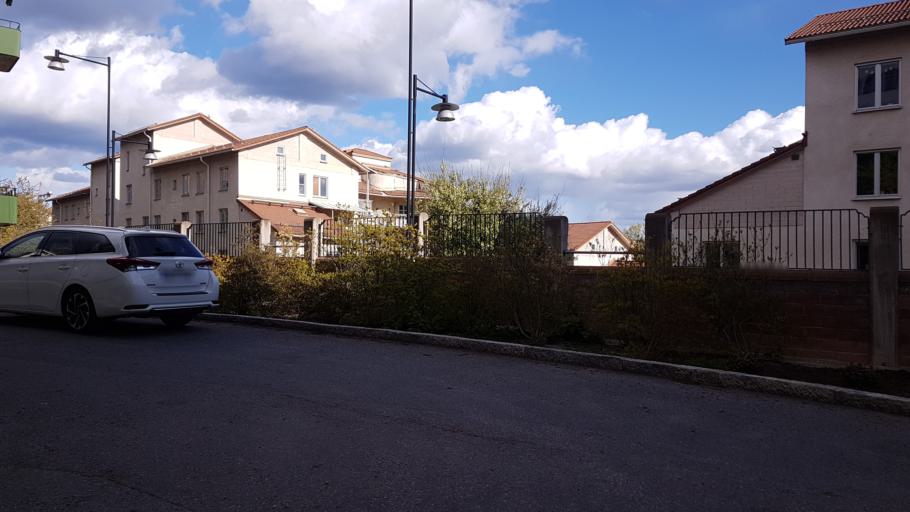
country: SE
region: Stockholm
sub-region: Stockholms Kommun
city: Arsta
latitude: 59.3160
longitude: 18.0435
